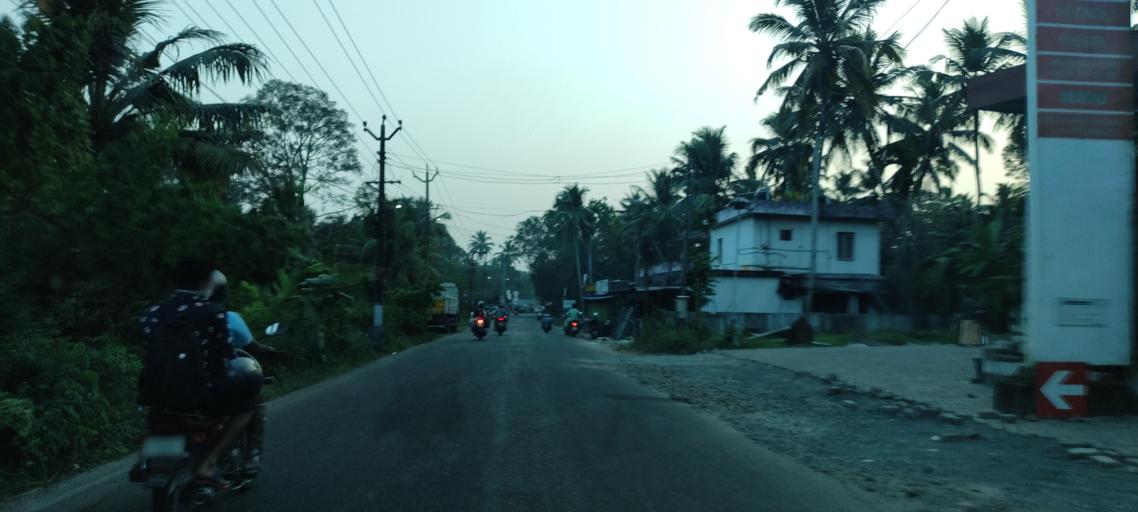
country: IN
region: Kerala
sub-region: Alappuzha
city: Kayankulam
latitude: 9.1268
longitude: 76.5025
